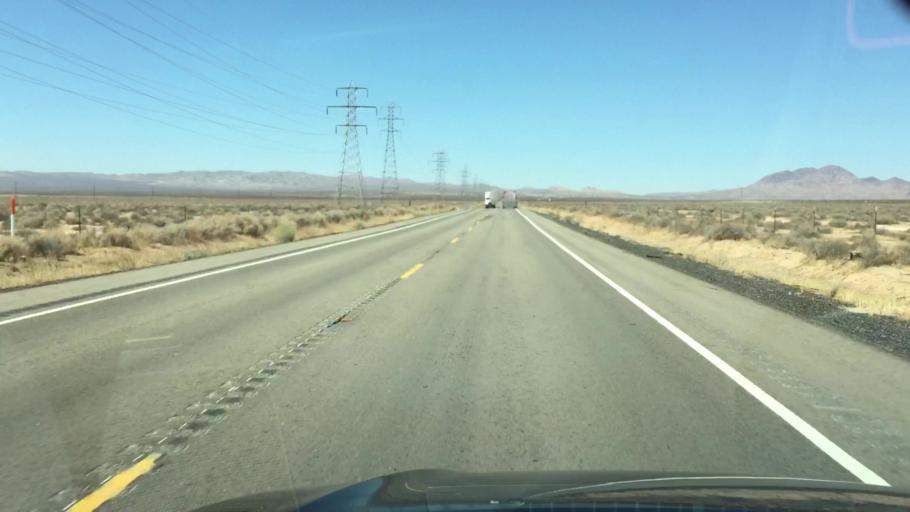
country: US
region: California
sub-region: Kern County
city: Boron
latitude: 35.2053
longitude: -117.6010
